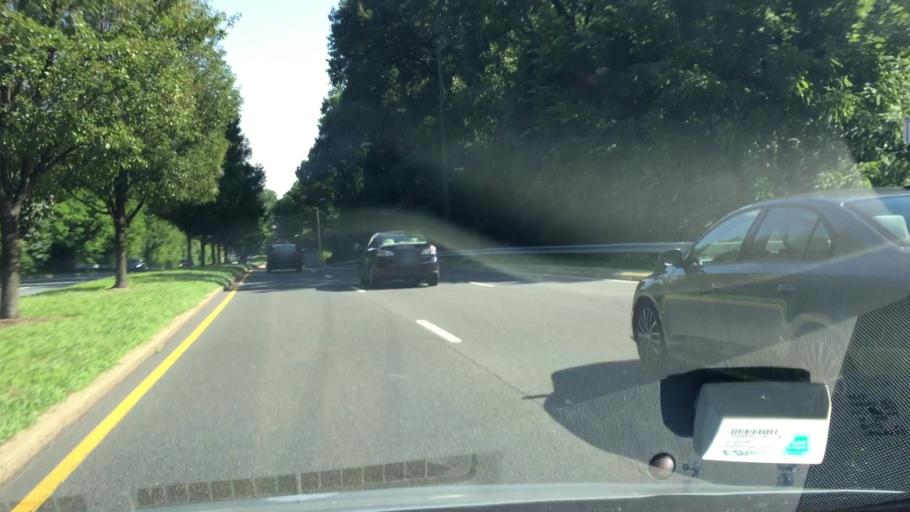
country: US
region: Maryland
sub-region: Montgomery County
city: North Kensington
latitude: 39.0447
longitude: -77.0763
